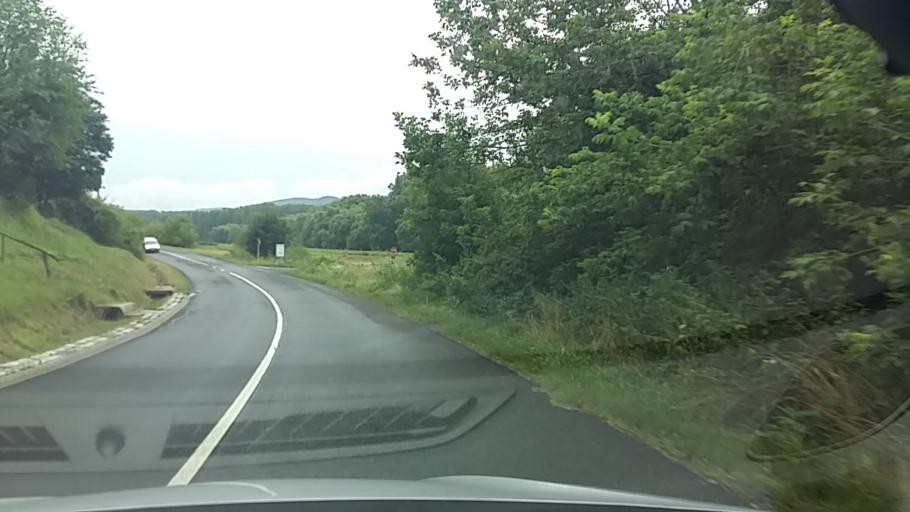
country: HU
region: Pest
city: Szob
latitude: 47.8467
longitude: 18.8228
